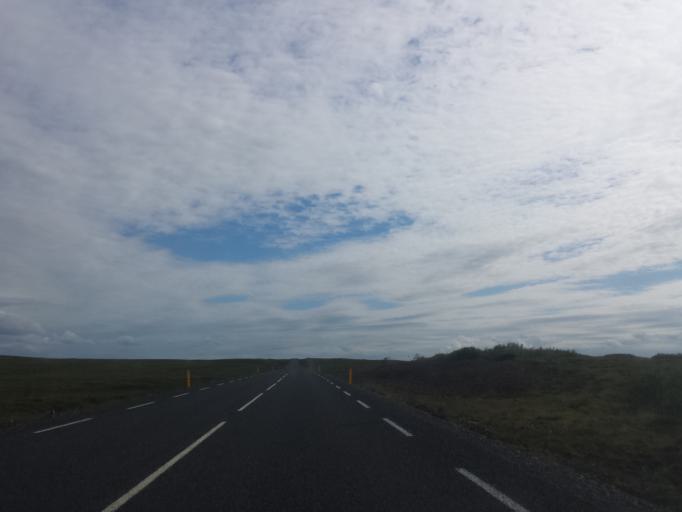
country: IS
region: Northeast
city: Husavik
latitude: 65.9921
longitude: -16.5647
